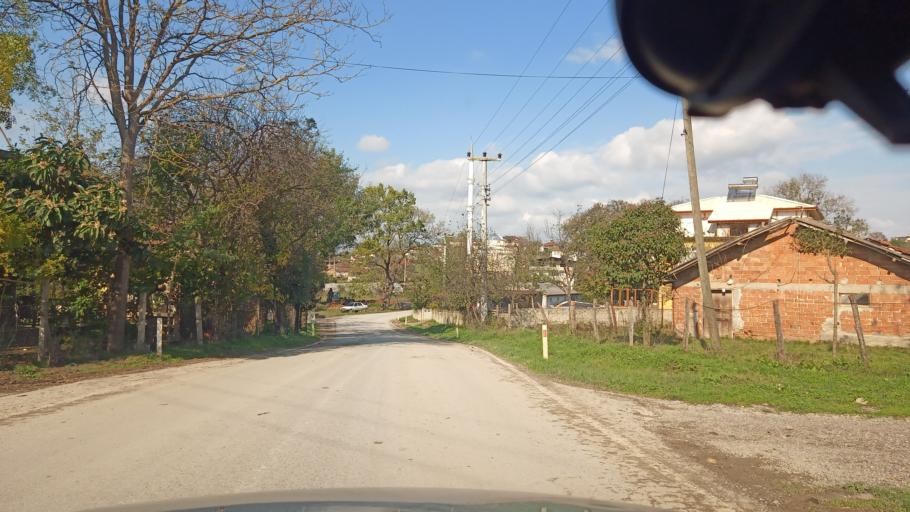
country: TR
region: Sakarya
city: Kaynarca
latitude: 41.0981
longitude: 30.4361
